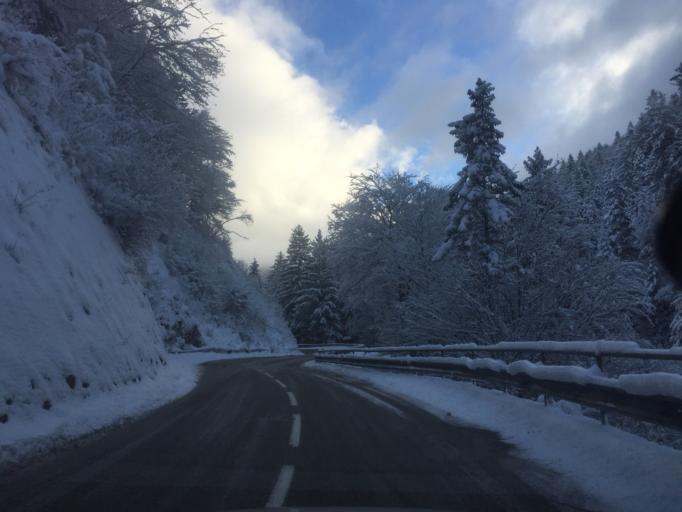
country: FR
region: Rhone-Alpes
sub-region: Departement de la Haute-Savoie
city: Saint-Paul-en-Chablais
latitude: 46.3338
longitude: 6.6140
